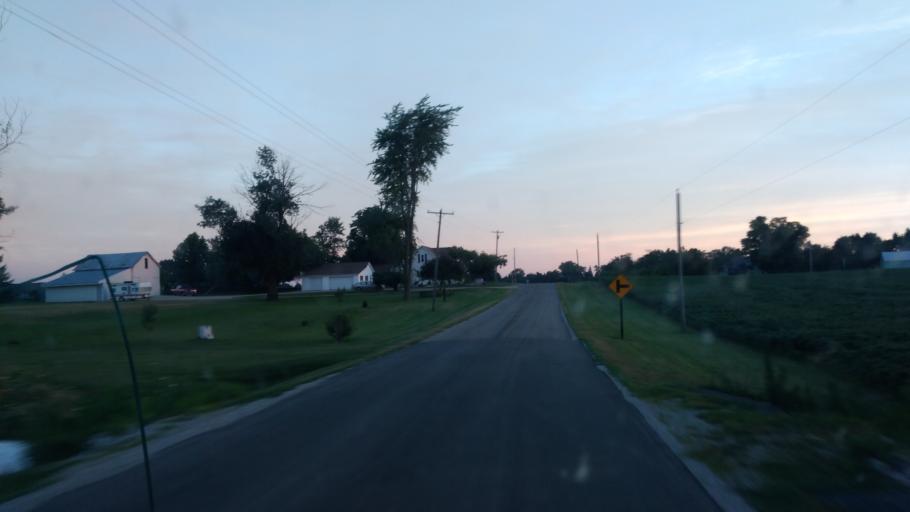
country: US
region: Indiana
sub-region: Wells County
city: Bluffton
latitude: 40.6824
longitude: -85.1359
